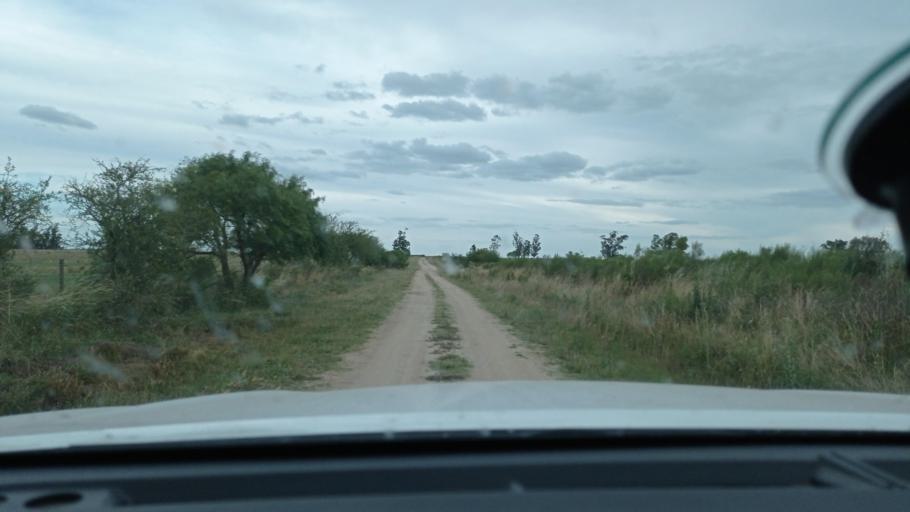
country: UY
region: Florida
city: Casupa
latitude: -34.1195
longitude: -55.8157
